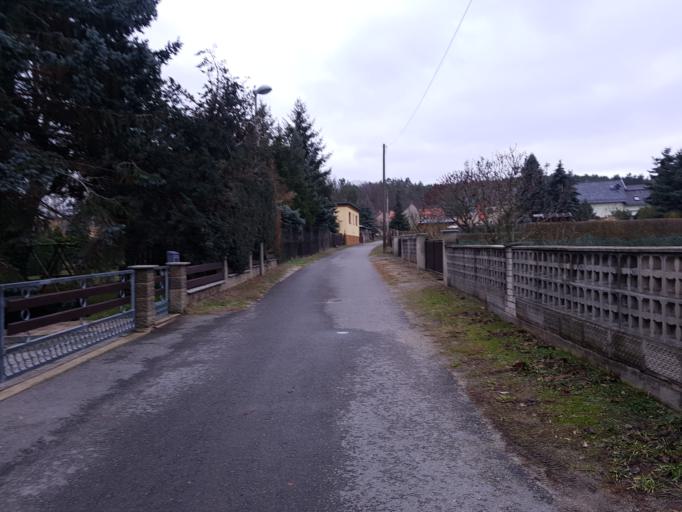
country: DE
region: Brandenburg
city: Groden
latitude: 51.4054
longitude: 13.5720
